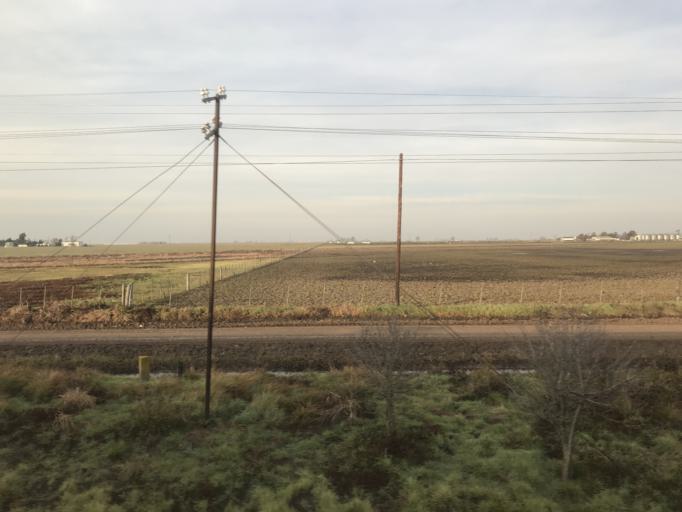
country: AR
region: Cordoba
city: Marcos Juarez
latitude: -32.6834
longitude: -62.1943
